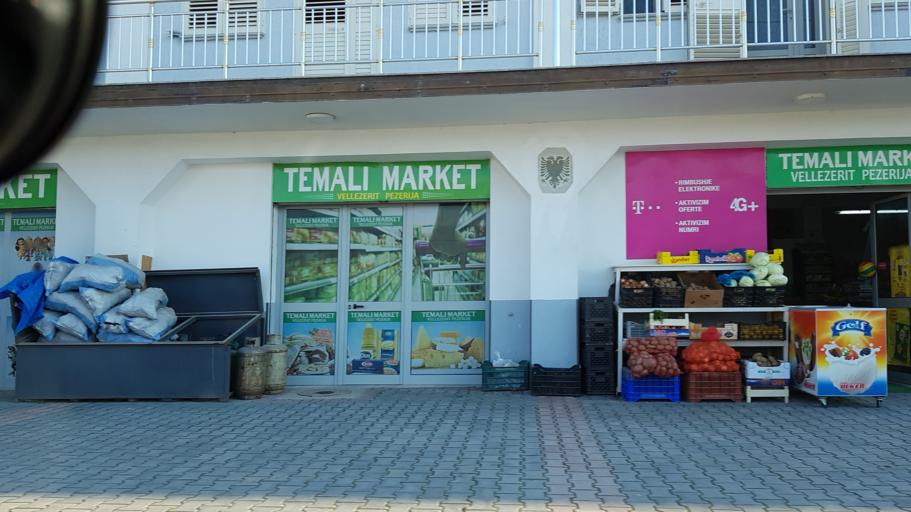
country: AL
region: Shkoder
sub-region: Rrethi i Shkodres
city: Shkoder
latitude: 42.0786
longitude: 19.4946
